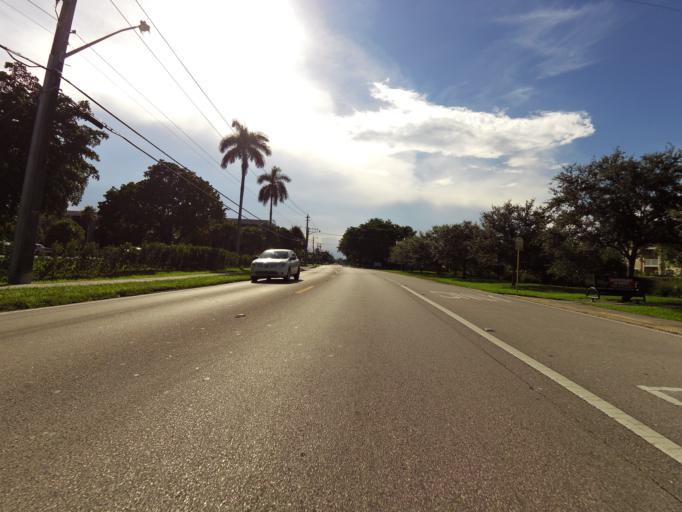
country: US
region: Florida
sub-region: Broward County
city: Davie
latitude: 26.0890
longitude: -80.2421
